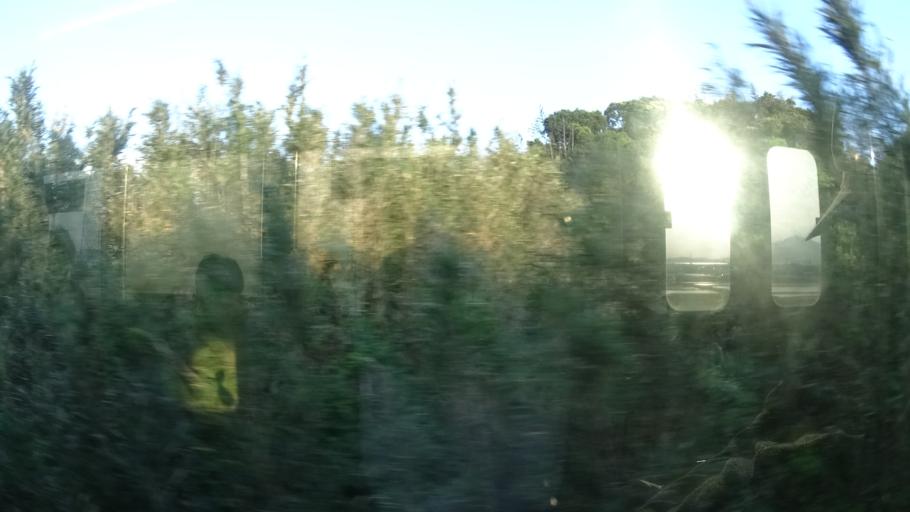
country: JP
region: Aichi
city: Tahara
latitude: 34.6827
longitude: 137.3221
